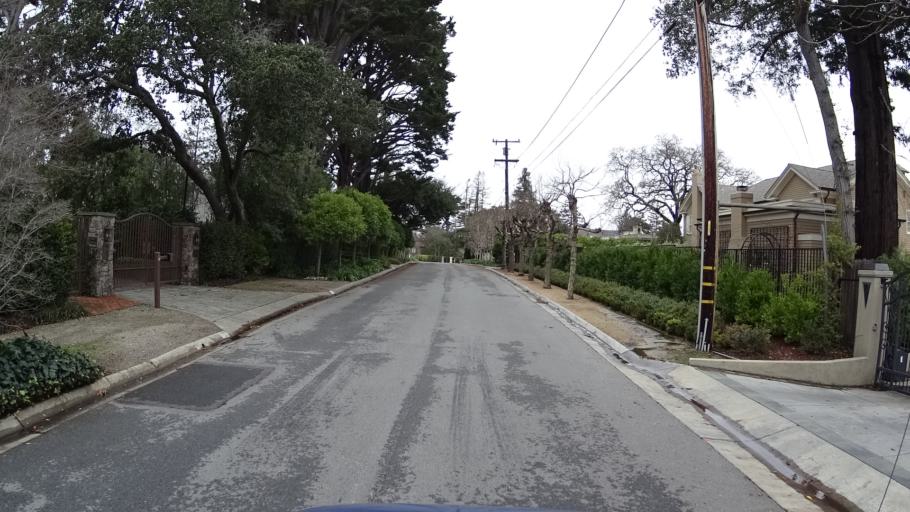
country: US
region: California
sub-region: San Mateo County
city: Burlingame
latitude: 37.5671
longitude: -122.3526
